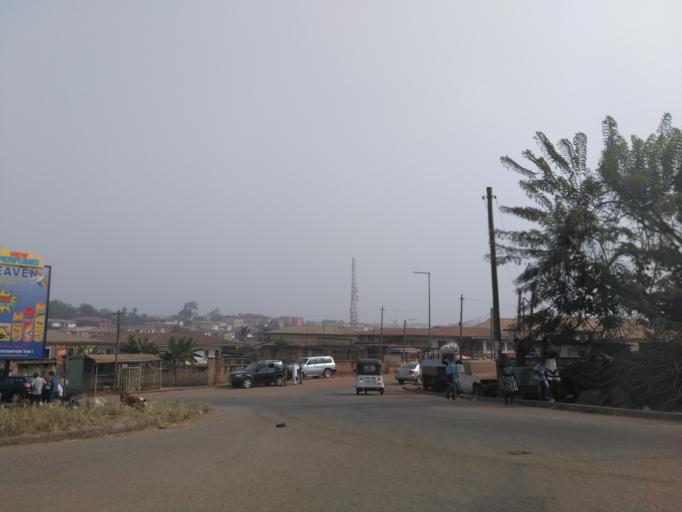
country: GH
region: Ashanti
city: Kumasi
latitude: 6.7079
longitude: -1.6244
